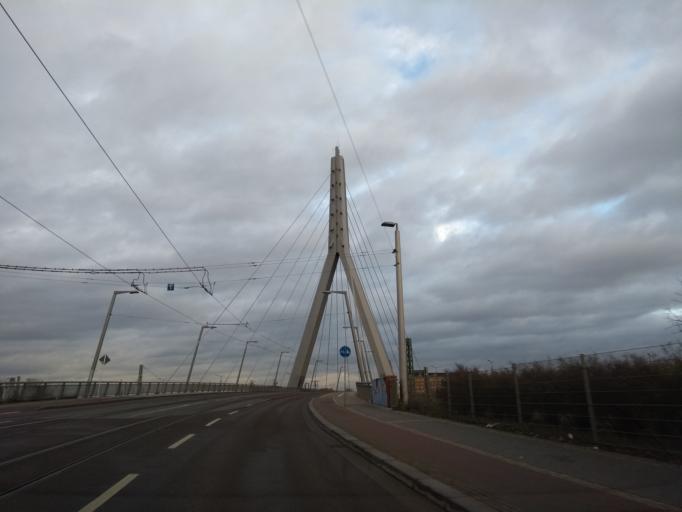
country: DE
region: Saxony-Anhalt
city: Halle (Saale)
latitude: 51.4899
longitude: 11.9890
